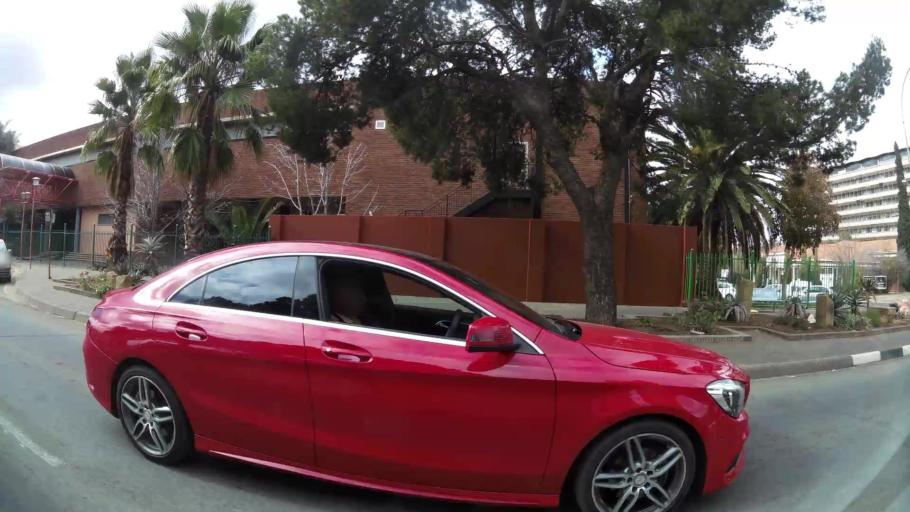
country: ZA
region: Orange Free State
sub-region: Mangaung Metropolitan Municipality
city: Bloemfontein
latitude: -29.1153
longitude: 26.2143
